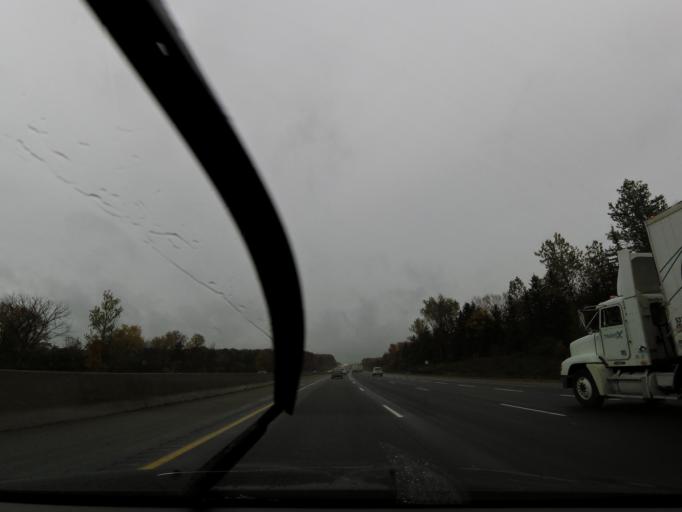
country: CA
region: Ontario
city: Cambridge
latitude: 43.4357
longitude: -80.2400
